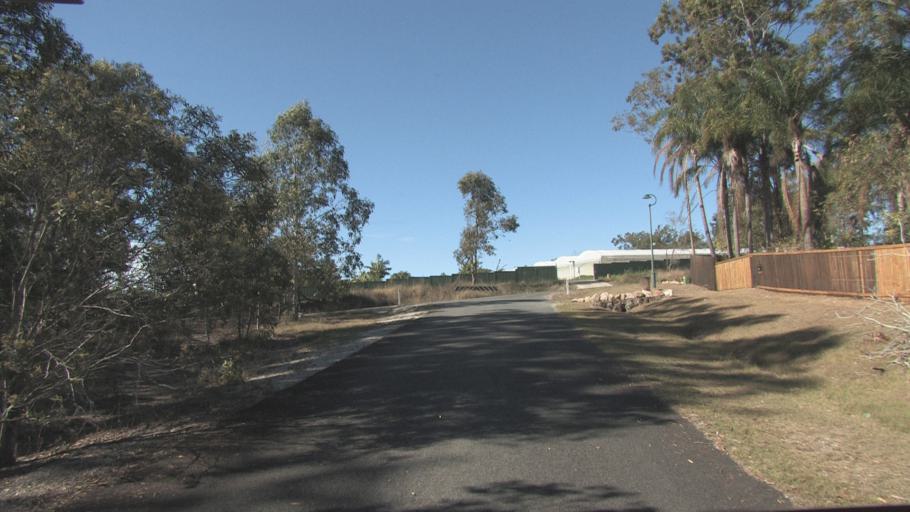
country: AU
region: Queensland
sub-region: Ipswich
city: Springfield Lakes
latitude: -27.7167
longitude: 152.9300
